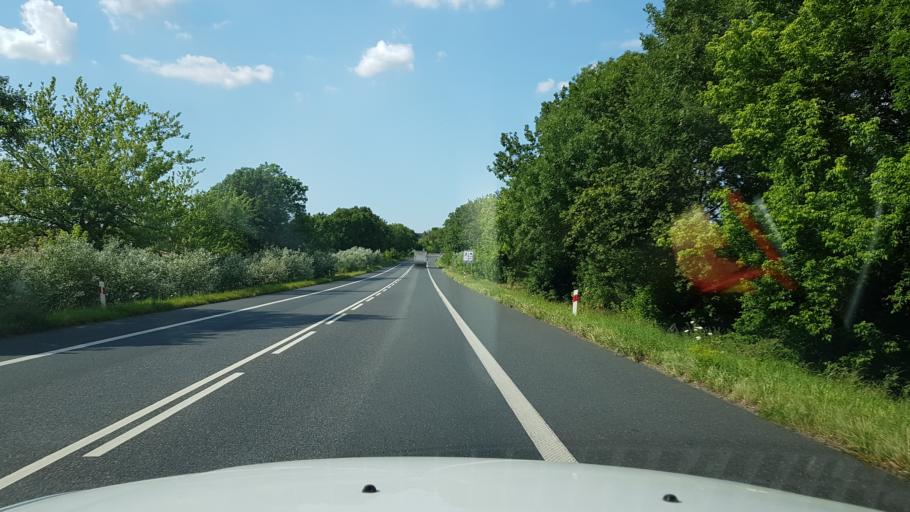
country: PL
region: West Pomeranian Voivodeship
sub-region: Powiat gryfinski
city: Stare Czarnowo
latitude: 53.2689
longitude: 14.7825
